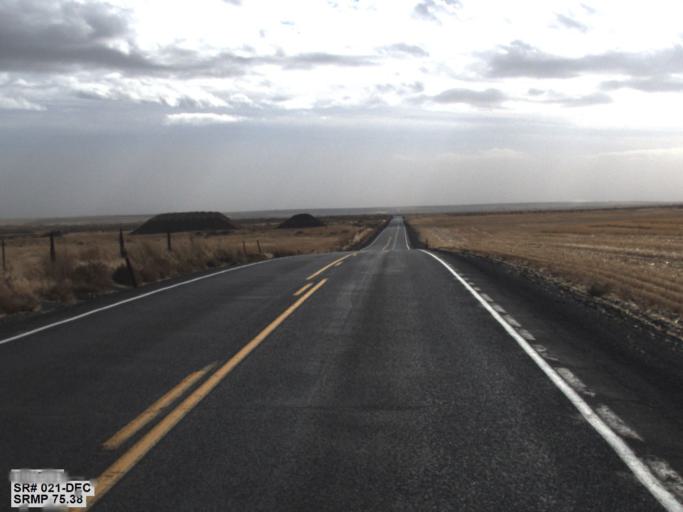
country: US
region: Washington
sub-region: Okanogan County
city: Coulee Dam
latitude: 47.5726
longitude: -118.7859
